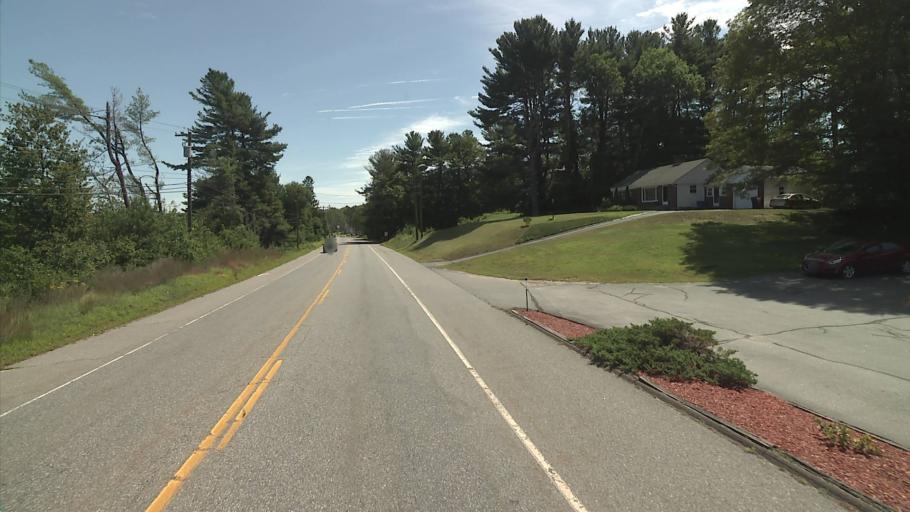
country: US
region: Connecticut
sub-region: Windham County
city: Killingly Center
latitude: 41.8473
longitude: -71.8993
